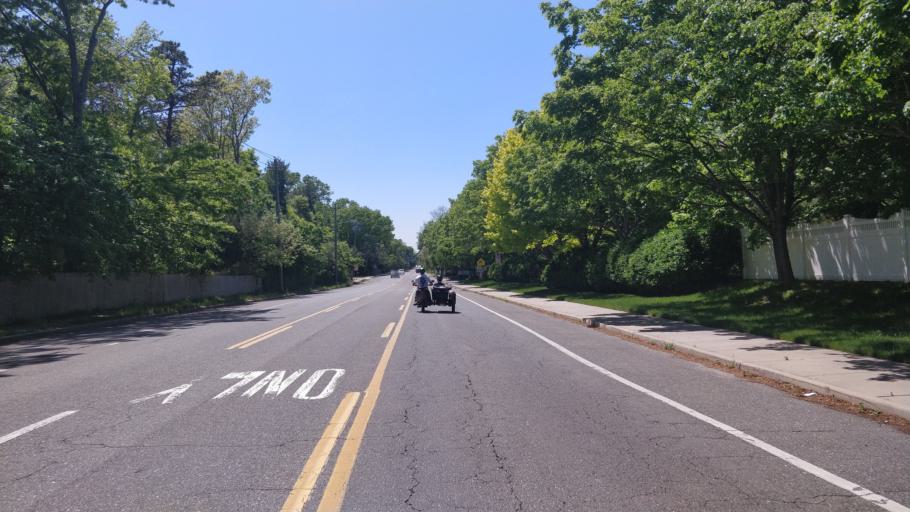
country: US
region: New York
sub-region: Suffolk County
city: Islandia
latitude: 40.8276
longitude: -73.1688
